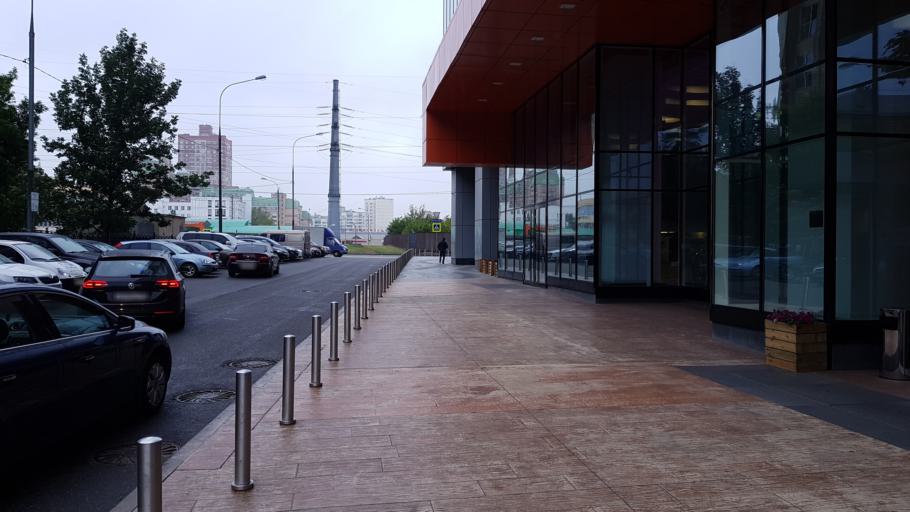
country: RU
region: Moskovskaya
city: Levoberezhnyy
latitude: 55.8397
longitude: 37.4903
